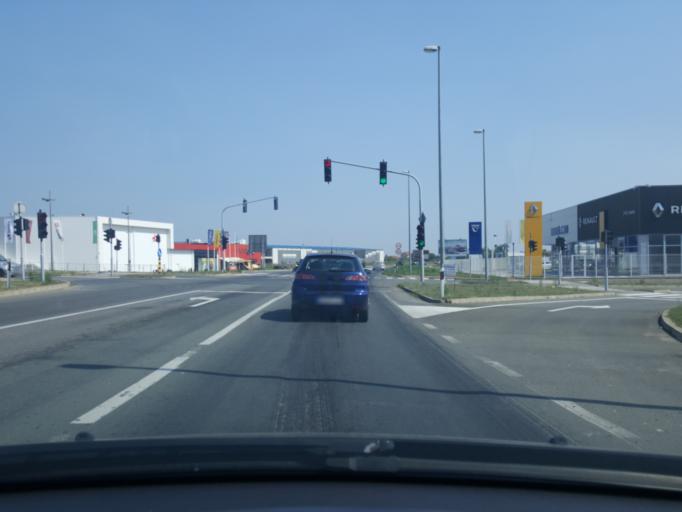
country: RS
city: Majur
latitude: 44.7543
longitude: 19.6605
